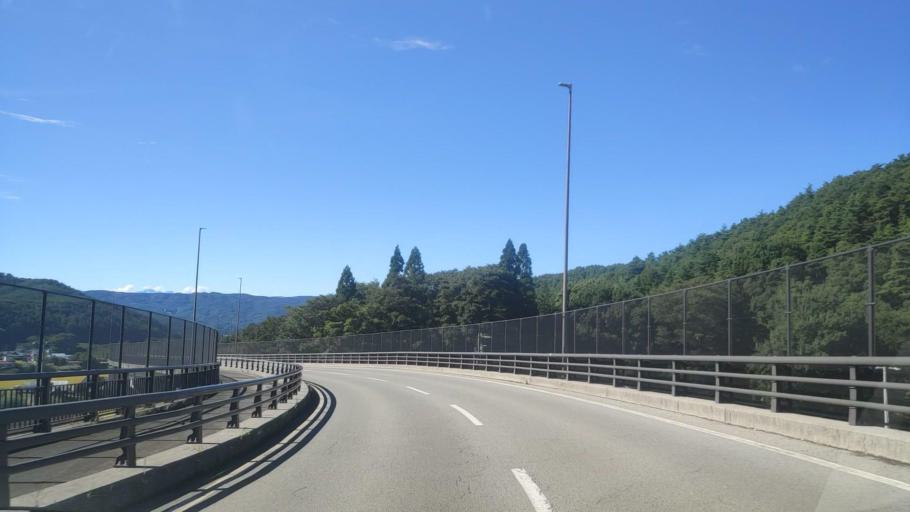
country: JP
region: Nagano
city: Chino
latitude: 35.9935
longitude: 138.2147
